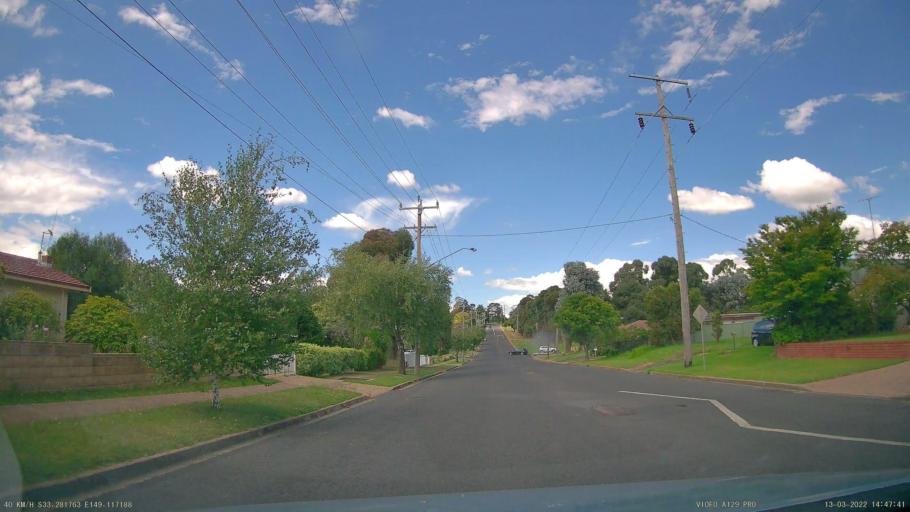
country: AU
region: New South Wales
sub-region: Orange Municipality
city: Orange
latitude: -33.2817
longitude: 149.1174
